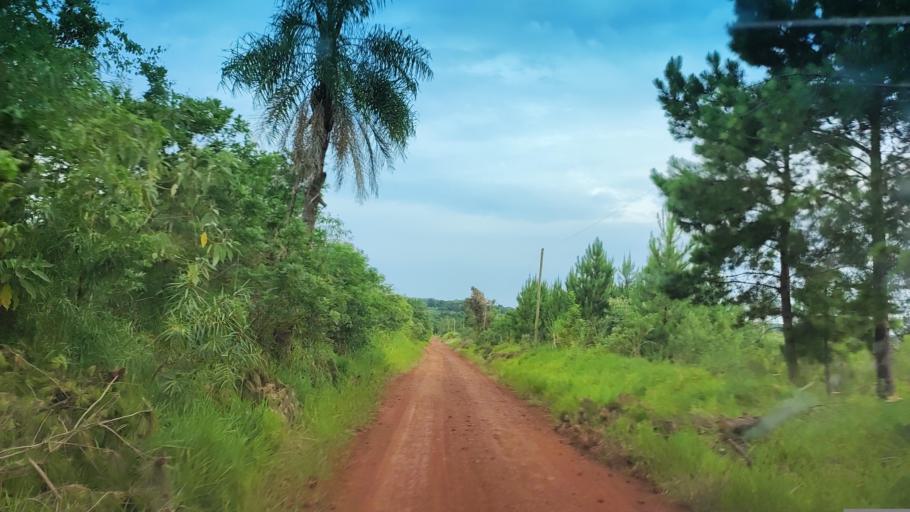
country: AR
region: Misiones
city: Gobernador Roca
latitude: -27.1681
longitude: -55.4529
